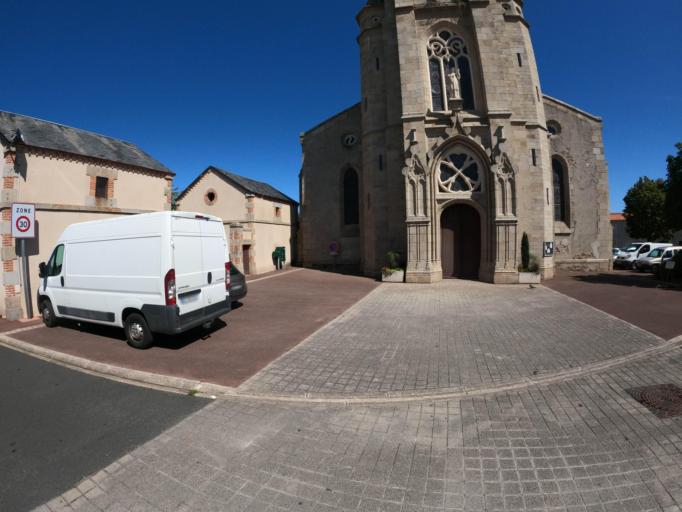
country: FR
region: Pays de la Loire
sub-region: Departement de la Vendee
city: La Boissiere-de-Montaigu
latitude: 46.9493
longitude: -1.1908
